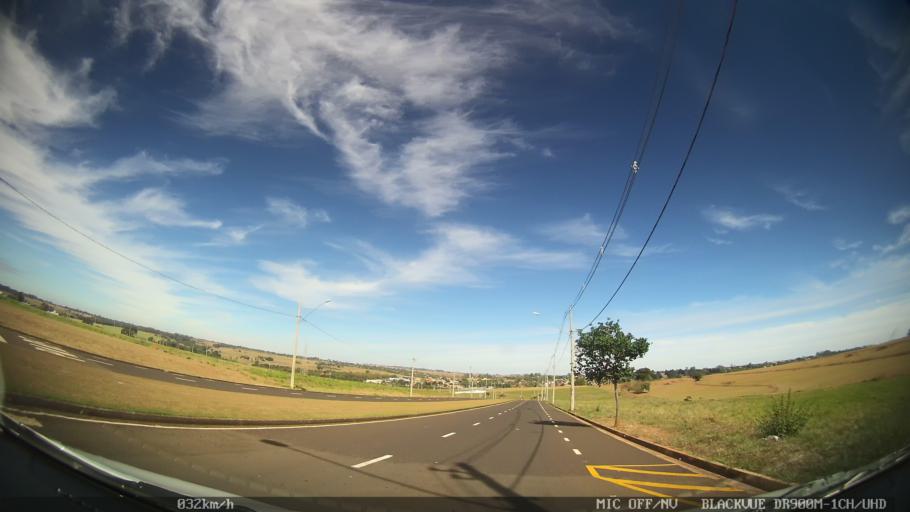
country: BR
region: Sao Paulo
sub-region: Sao Jose Do Rio Preto
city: Sao Jose do Rio Preto
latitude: -20.8515
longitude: -49.3794
